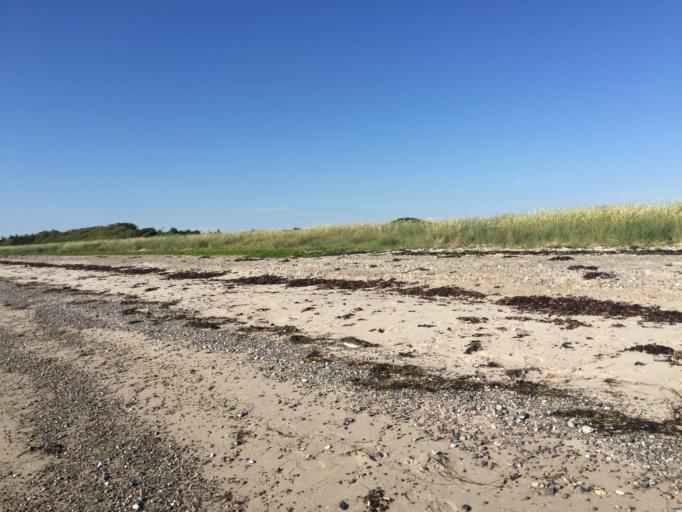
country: DK
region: Zealand
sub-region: Slagelse Kommune
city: Korsor
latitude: 55.2260
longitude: 11.1717
